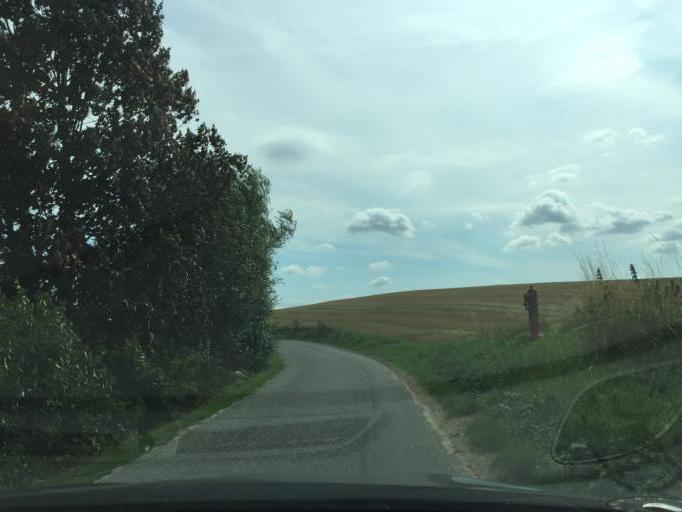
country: DK
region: South Denmark
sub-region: Assens Kommune
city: Tommerup Stationsby
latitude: 55.4071
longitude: 10.2296
